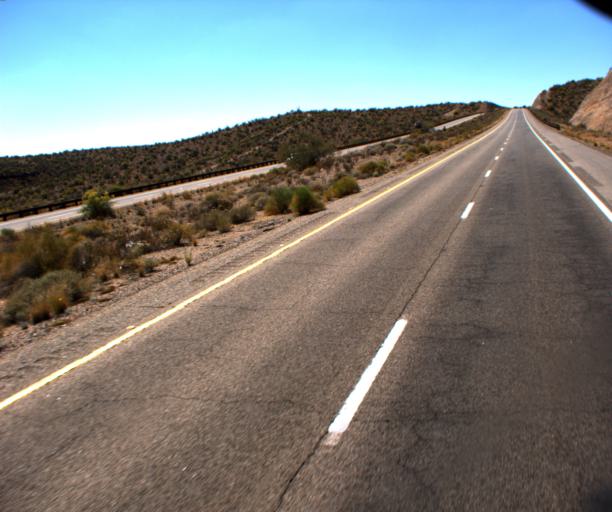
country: US
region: Arizona
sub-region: Yavapai County
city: Bagdad
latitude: 34.5825
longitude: -113.4983
